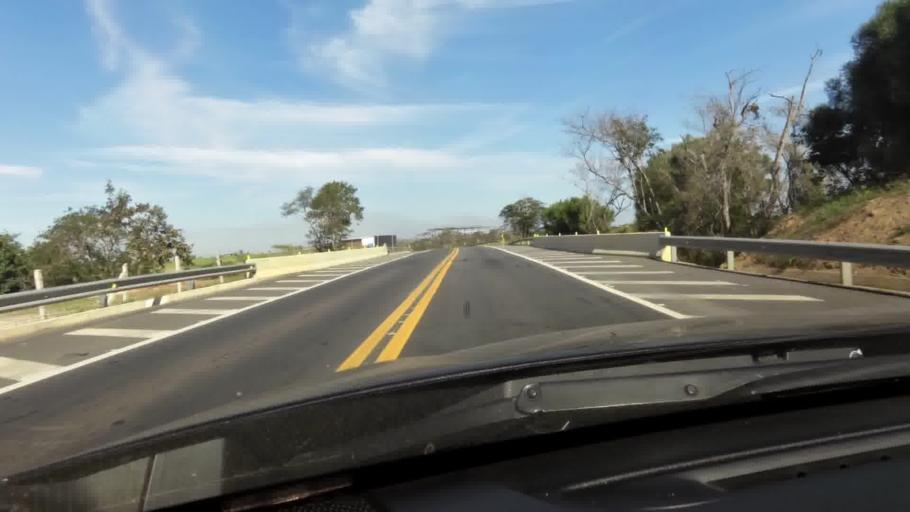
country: BR
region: Rio de Janeiro
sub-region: Campos Dos Goytacazes
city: Campos
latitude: -21.5352
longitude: -41.3415
